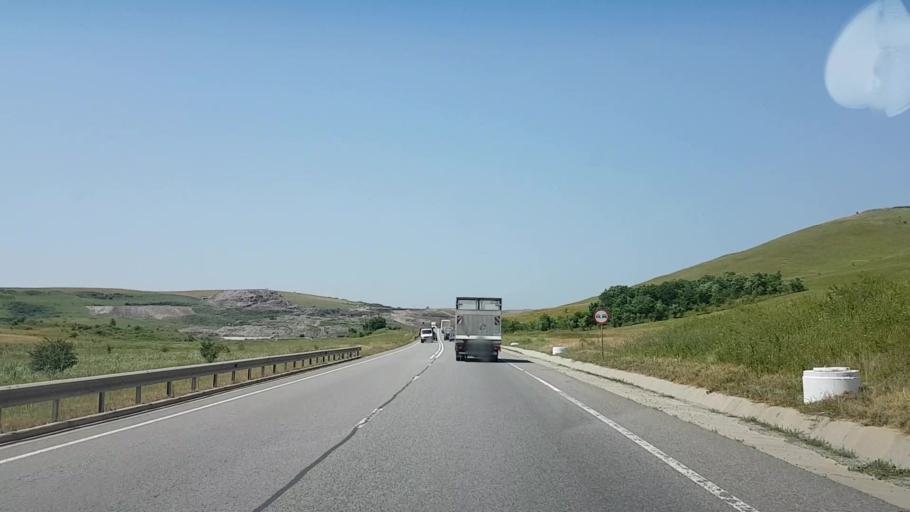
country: RO
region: Cluj
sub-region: Comuna Apahida
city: Dezmir
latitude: 46.7572
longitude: 23.6982
